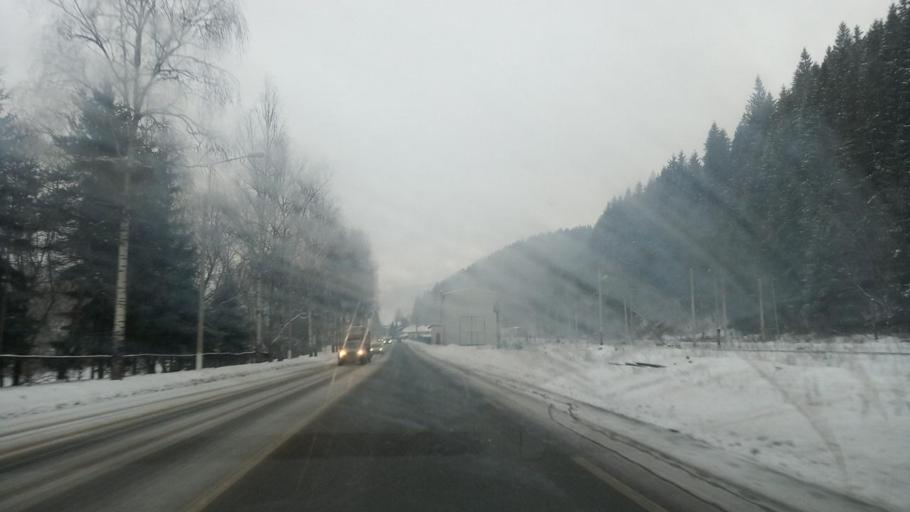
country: RO
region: Suceava
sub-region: Municipiul Vatra Dornei
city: Vatra Dornei
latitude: 47.3560
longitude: 25.3544
